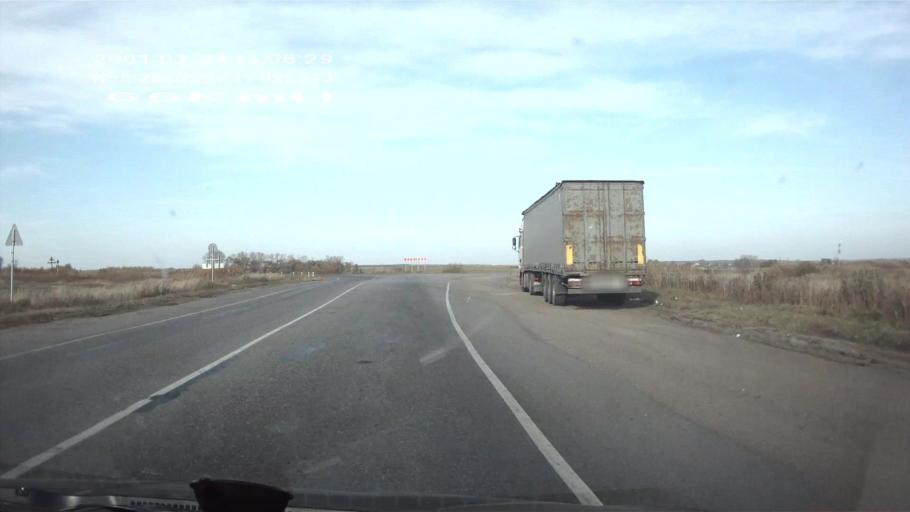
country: RU
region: Chuvashia
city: Ibresi
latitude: 55.2847
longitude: 47.0802
